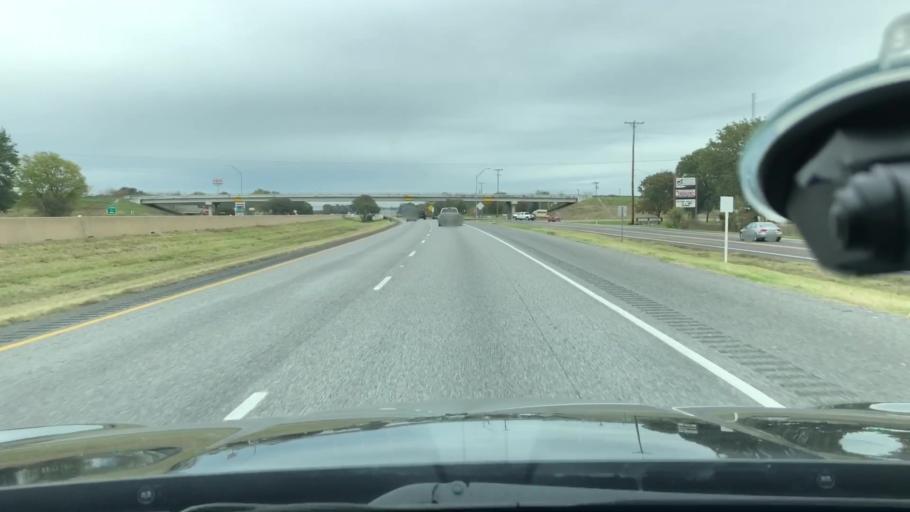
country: US
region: Texas
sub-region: Hunt County
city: Greenville
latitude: 33.1333
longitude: -96.0588
